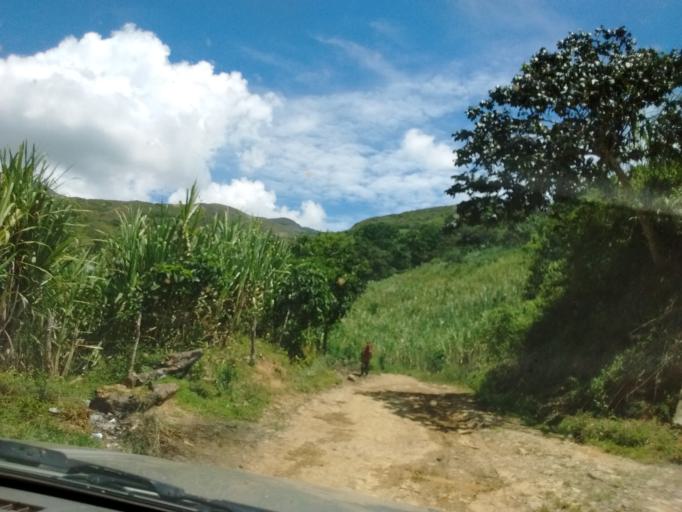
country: CO
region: Cauca
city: Villa Rica
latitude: 2.6309
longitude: -76.7708
